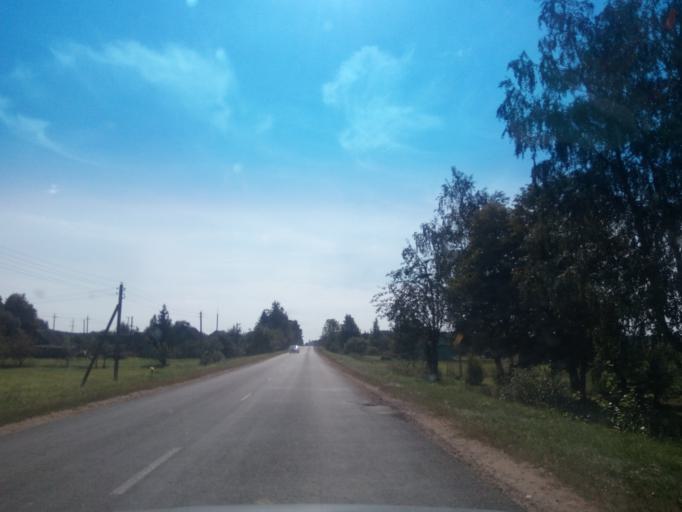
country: BY
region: Vitebsk
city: Vyerkhnyadzvinsk
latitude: 55.8264
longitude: 27.7354
